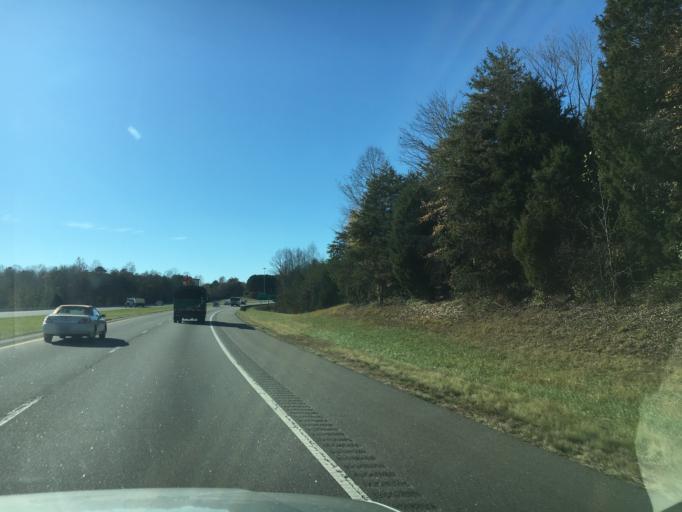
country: US
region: North Carolina
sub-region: Catawba County
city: Conover
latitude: 35.7041
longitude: -81.2538
